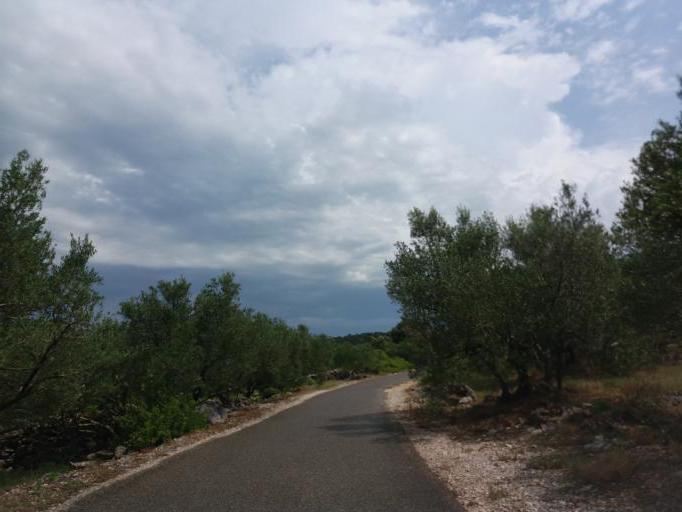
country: HR
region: Zadarska
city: Sali
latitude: 43.9344
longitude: 15.1397
